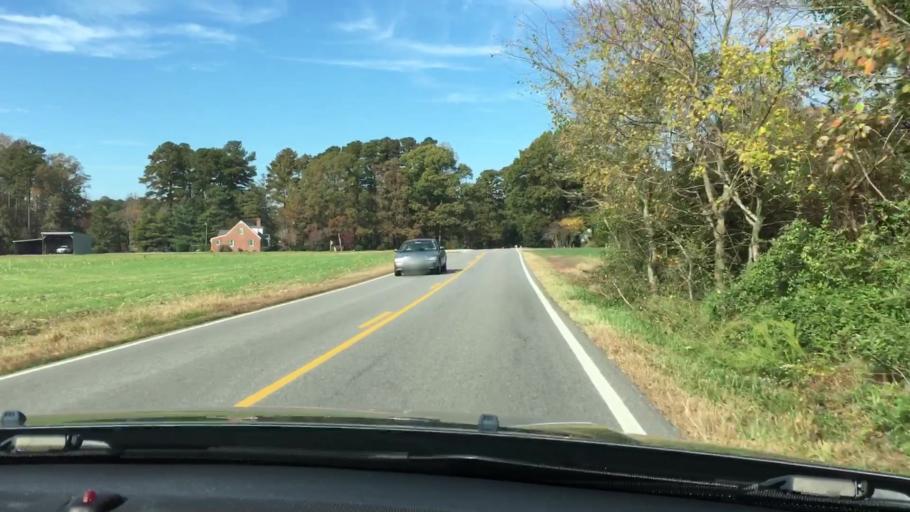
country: US
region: Virginia
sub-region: King William County
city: West Point
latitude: 37.5172
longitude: -76.8217
